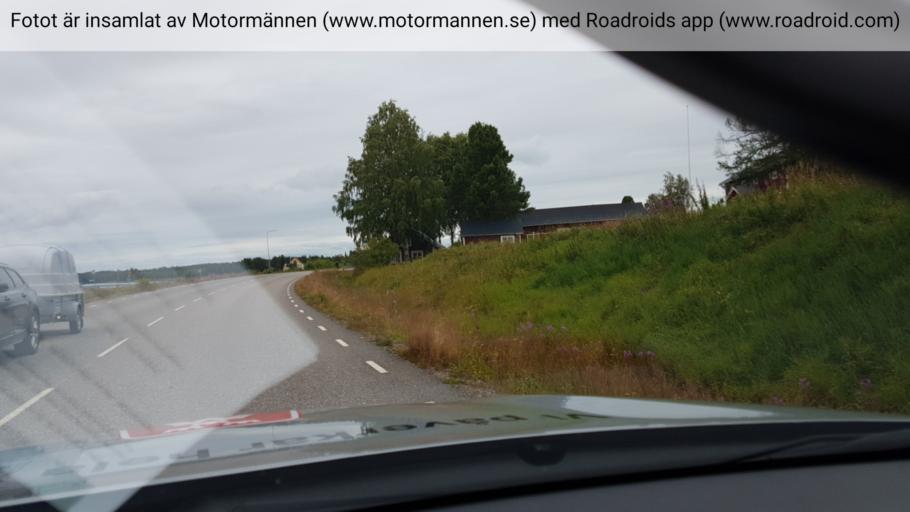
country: SE
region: Norrbotten
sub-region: Pajala Kommun
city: Pajala
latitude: 67.1670
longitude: 22.6153
